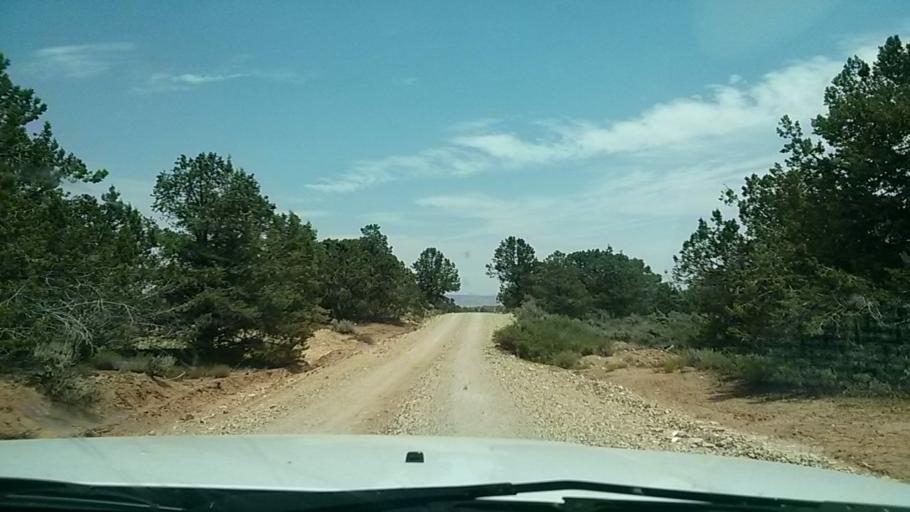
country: US
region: Utah
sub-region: Washington County
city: Washington
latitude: 37.2348
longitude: -113.4609
